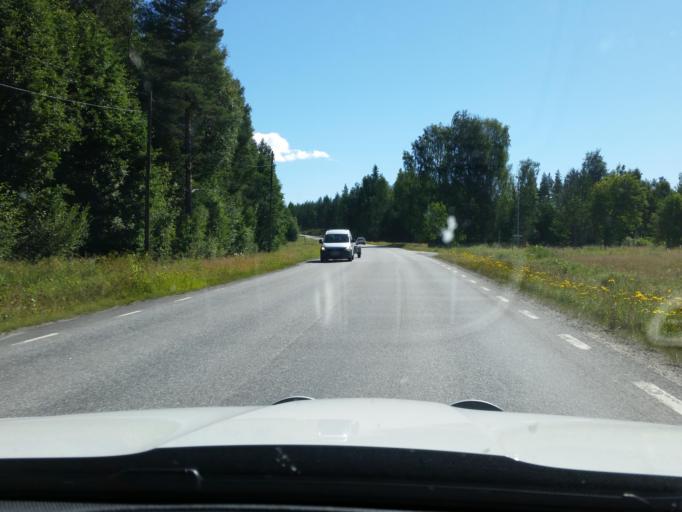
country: SE
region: Norrbotten
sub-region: Pitea Kommun
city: Bergsviken
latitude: 65.3160
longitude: 21.2974
